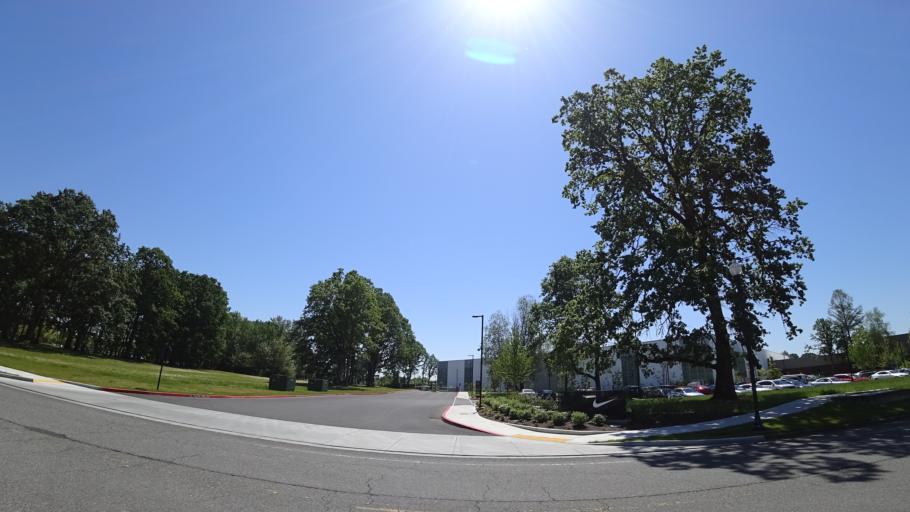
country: US
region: Oregon
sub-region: Washington County
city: Beaverton
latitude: 45.4978
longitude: -122.8151
